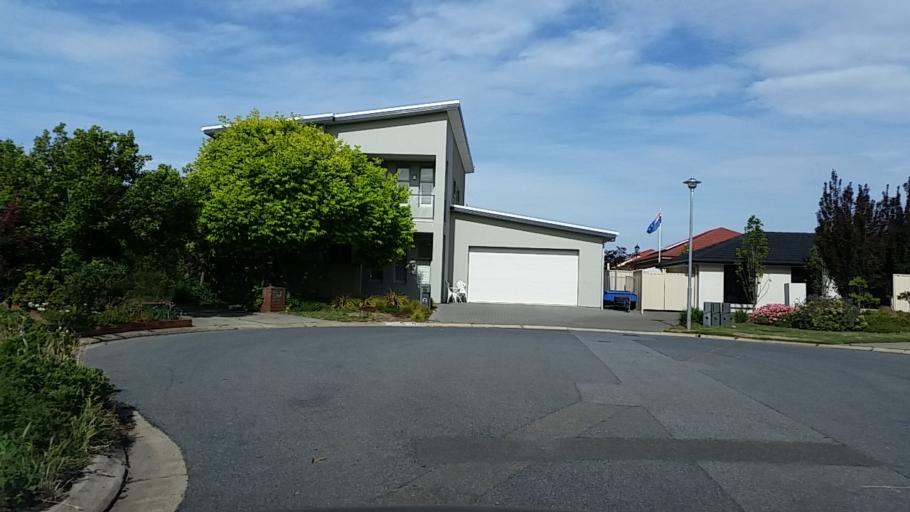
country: AU
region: South Australia
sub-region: Charles Sturt
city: Grange
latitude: -34.8950
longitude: 138.4976
